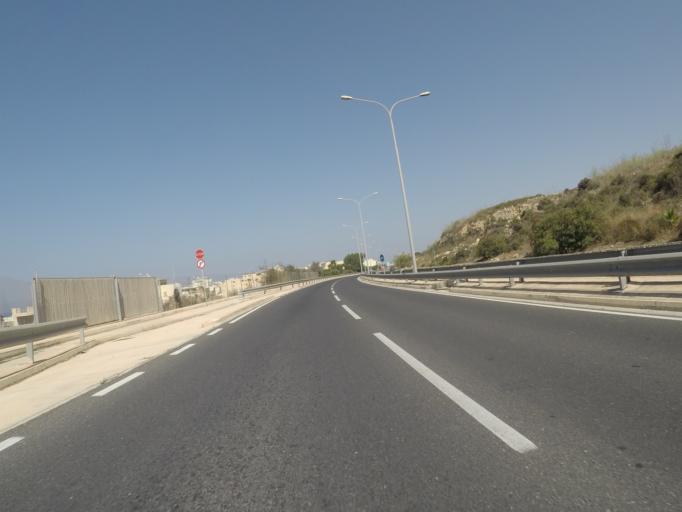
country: MT
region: Saint Paul's Bay
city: San Pawl il-Bahar
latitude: 35.9470
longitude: 14.3996
